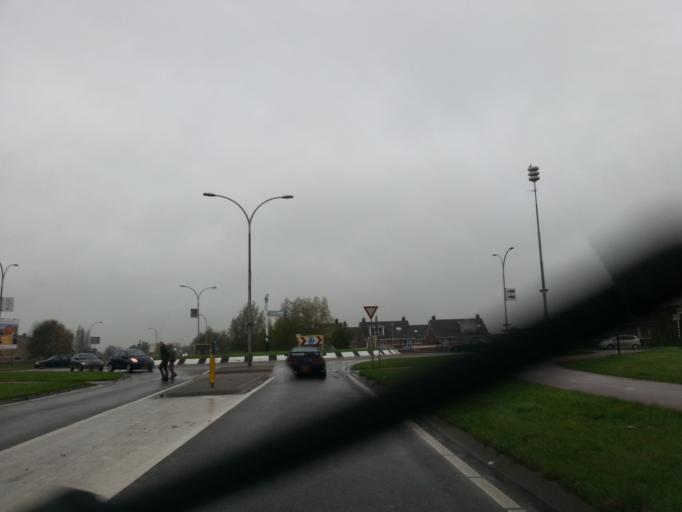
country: NL
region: South Holland
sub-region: Gemeente Lansingerland
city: Berkel en Rodenrijs
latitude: 51.9928
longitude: 4.4660
